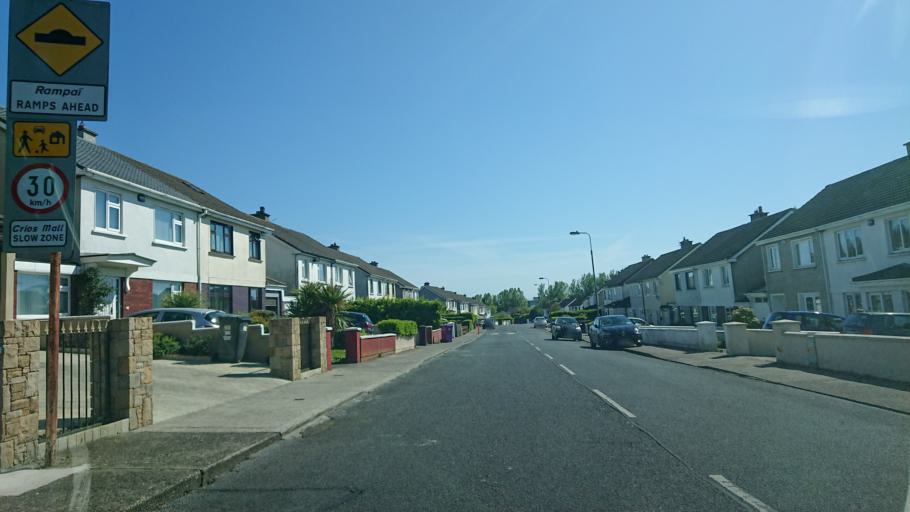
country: IE
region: Munster
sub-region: Waterford
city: Waterford
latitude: 52.2533
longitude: -7.1444
